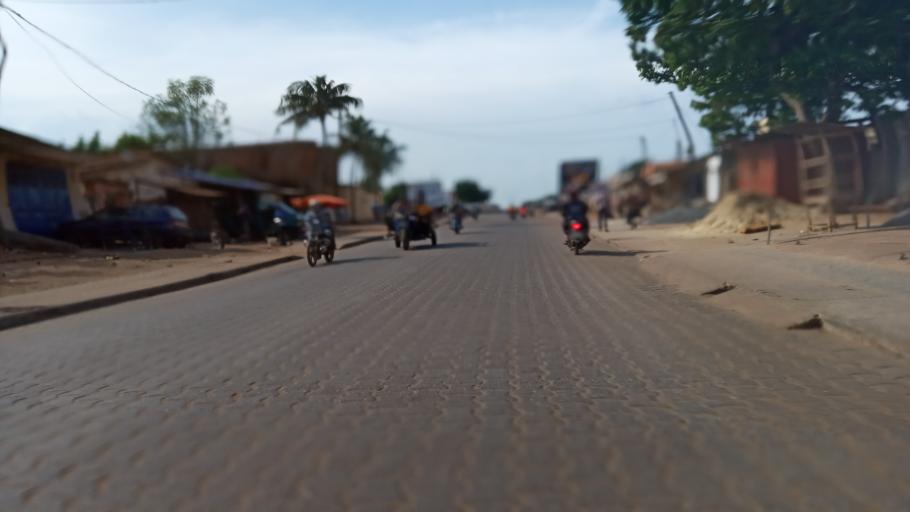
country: TG
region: Maritime
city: Lome
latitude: 6.1603
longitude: 1.2662
